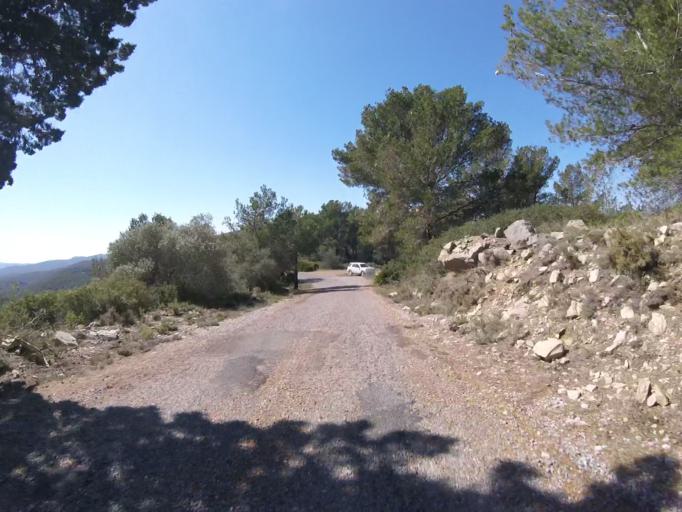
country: ES
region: Valencia
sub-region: Provincia de Castello
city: Cervera del Maestre
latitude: 40.4098
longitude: 0.1990
